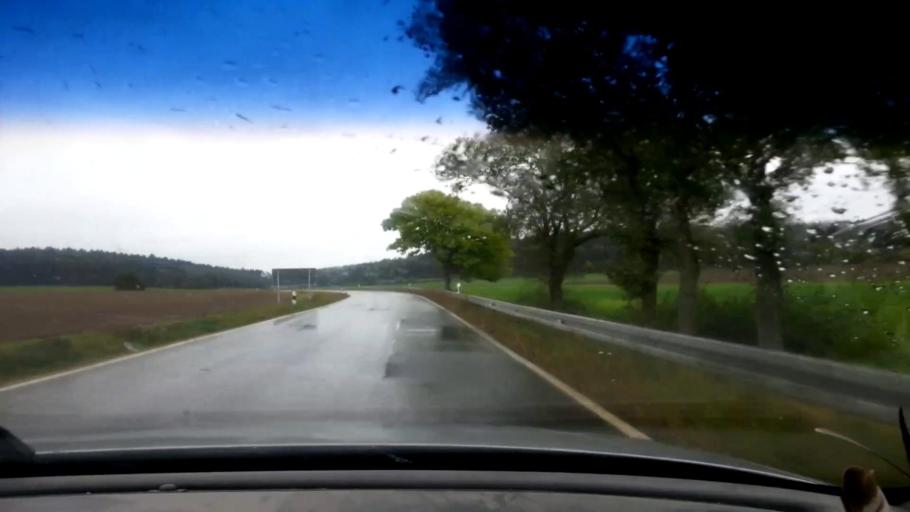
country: DE
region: Bavaria
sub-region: Upper Franconia
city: Konigsfeld
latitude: 49.9437
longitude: 11.1557
